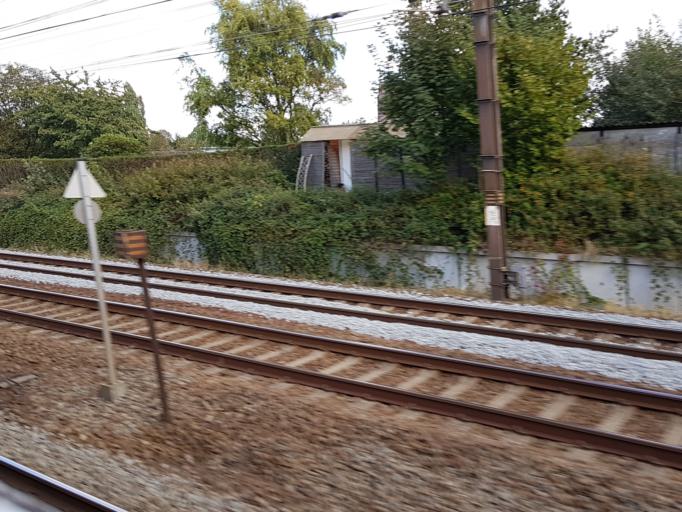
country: BE
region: Flanders
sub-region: Provincie Antwerpen
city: Lint
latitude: 51.1281
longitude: 4.4799
